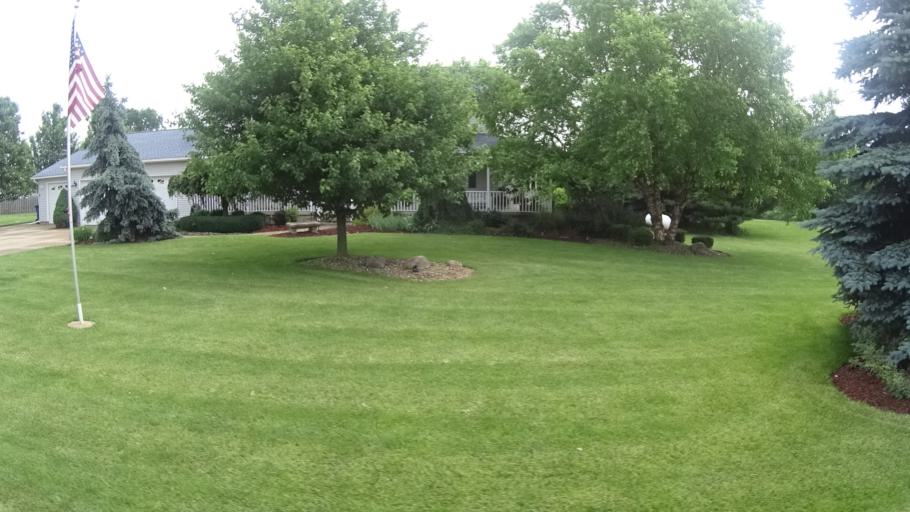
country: US
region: Ohio
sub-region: Erie County
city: Sandusky
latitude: 41.3599
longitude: -82.7583
